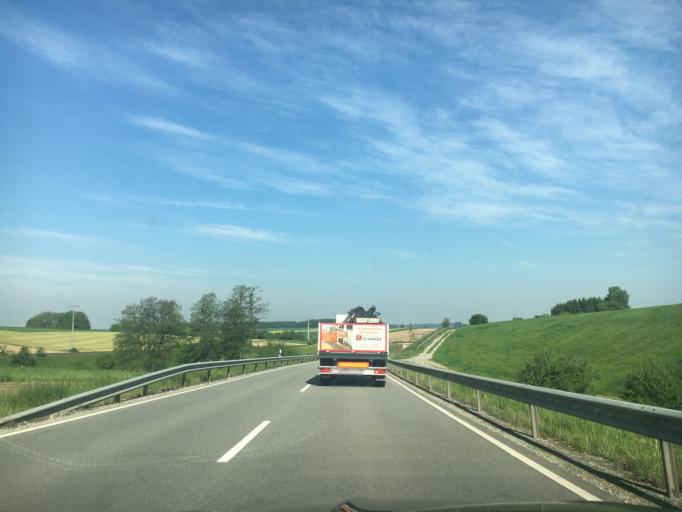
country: DE
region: Bavaria
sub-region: Upper Bavaria
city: Neumarkt-Sankt Veit
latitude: 48.3463
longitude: 12.4981
